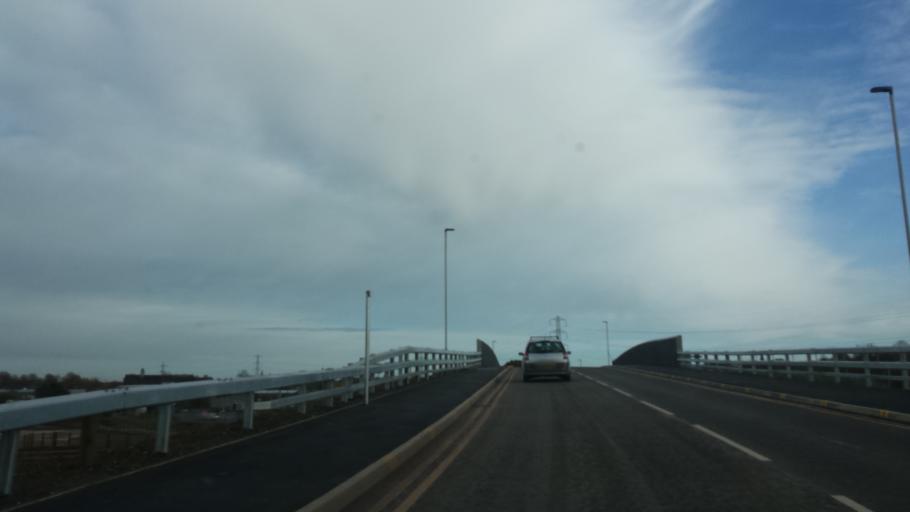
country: GB
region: England
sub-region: Hertfordshire
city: Watford
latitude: 51.6468
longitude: -0.3998
